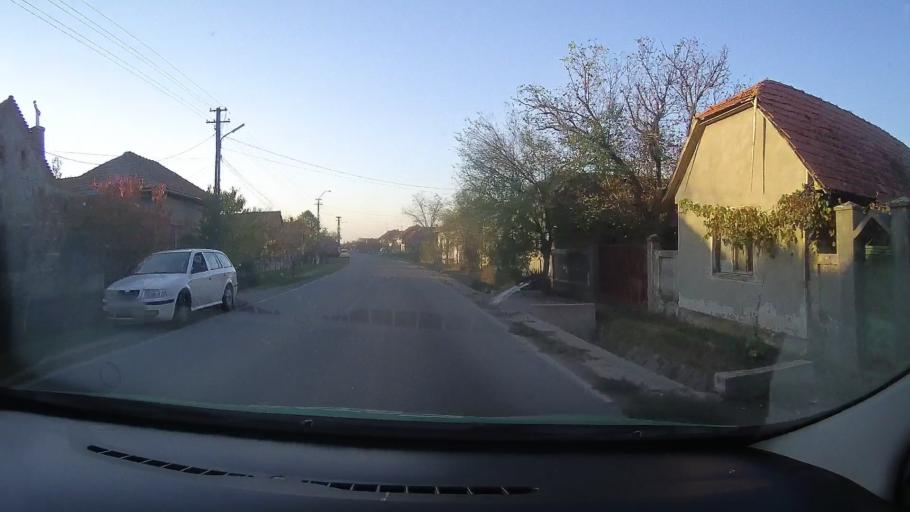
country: RO
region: Timis
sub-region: Comuna Traian Vuia
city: Traian Vuia
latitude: 45.7926
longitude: 22.0721
